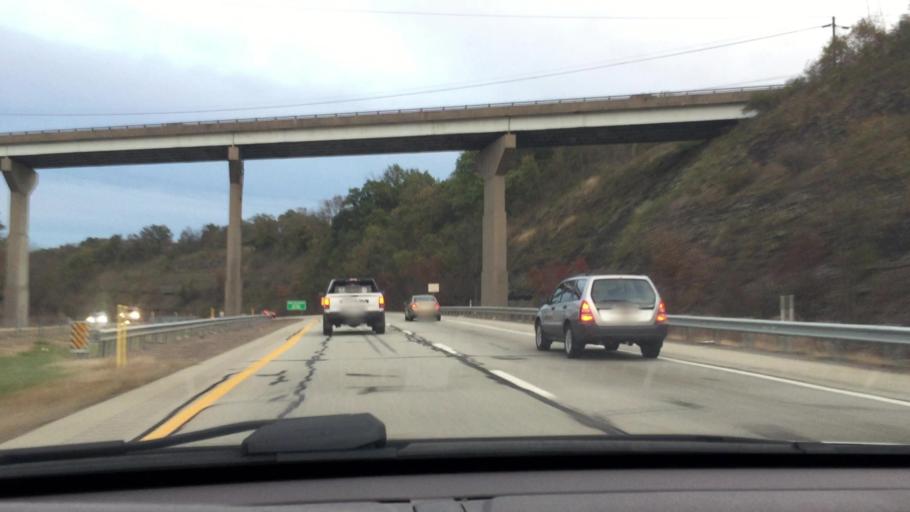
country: US
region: Pennsylvania
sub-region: Westmoreland County
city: Arnold
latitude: 40.5710
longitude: -79.7915
